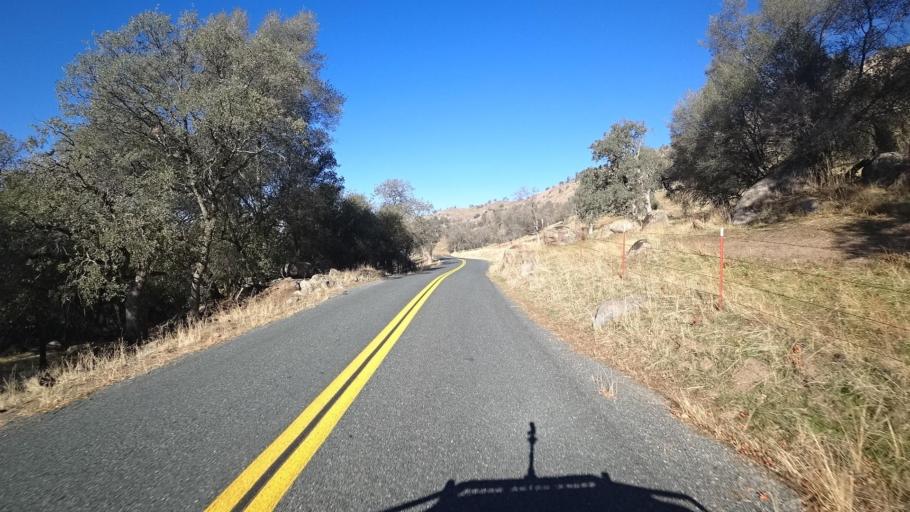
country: US
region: California
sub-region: Kern County
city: Alta Sierra
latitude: 35.7875
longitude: -118.7910
